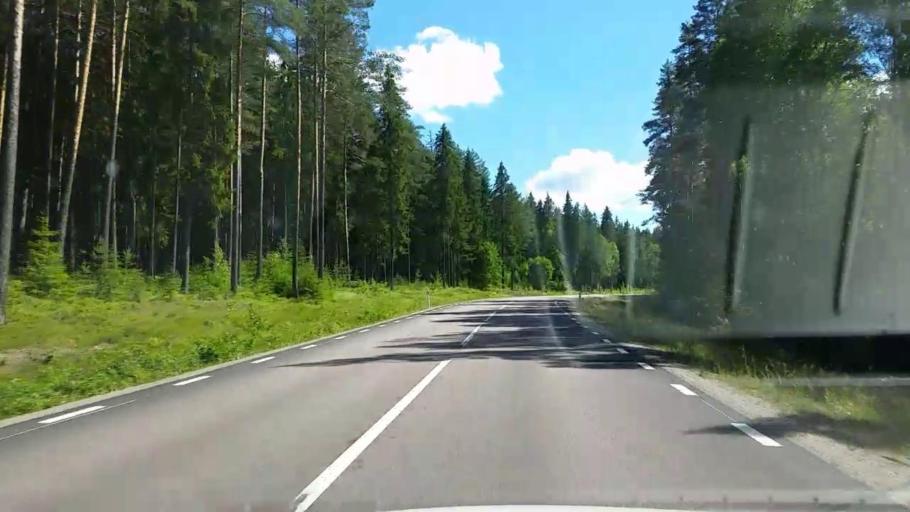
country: SE
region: Dalarna
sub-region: Faluns Kommun
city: Svardsjo
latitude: 60.7743
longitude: 15.7547
